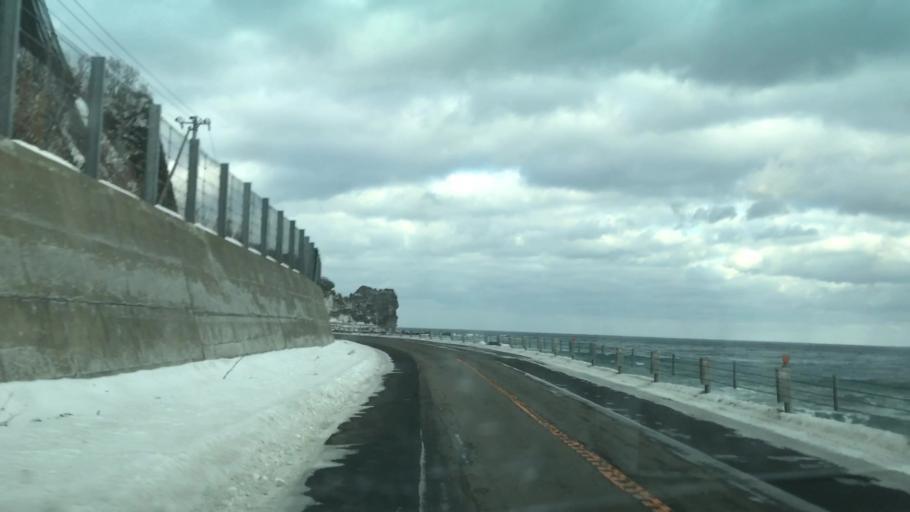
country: JP
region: Hokkaido
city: Iwanai
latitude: 43.3295
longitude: 140.4204
